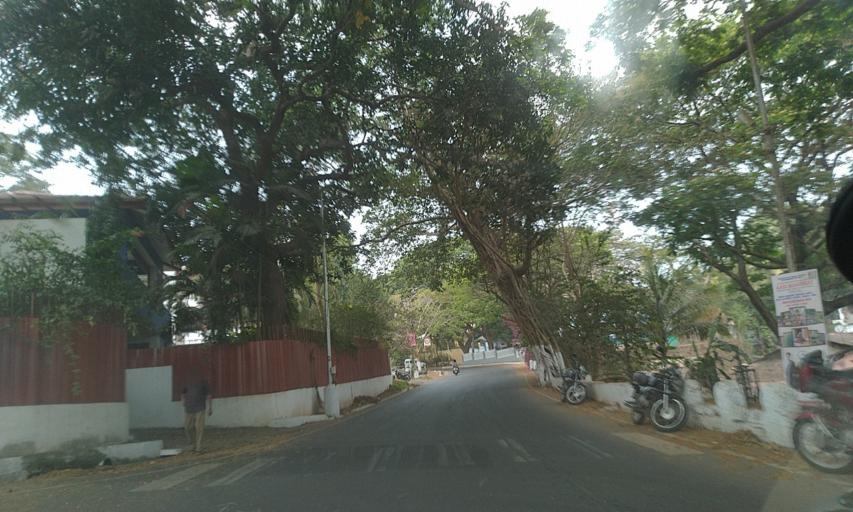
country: IN
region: Goa
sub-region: North Goa
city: Panaji
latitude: 15.4934
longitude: 73.8251
